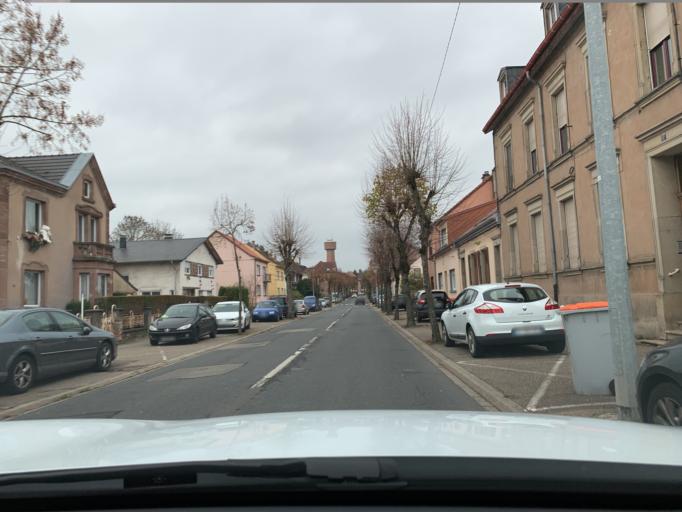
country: FR
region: Lorraine
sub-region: Departement de la Moselle
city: Sarreguemines
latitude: 49.1054
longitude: 7.0588
